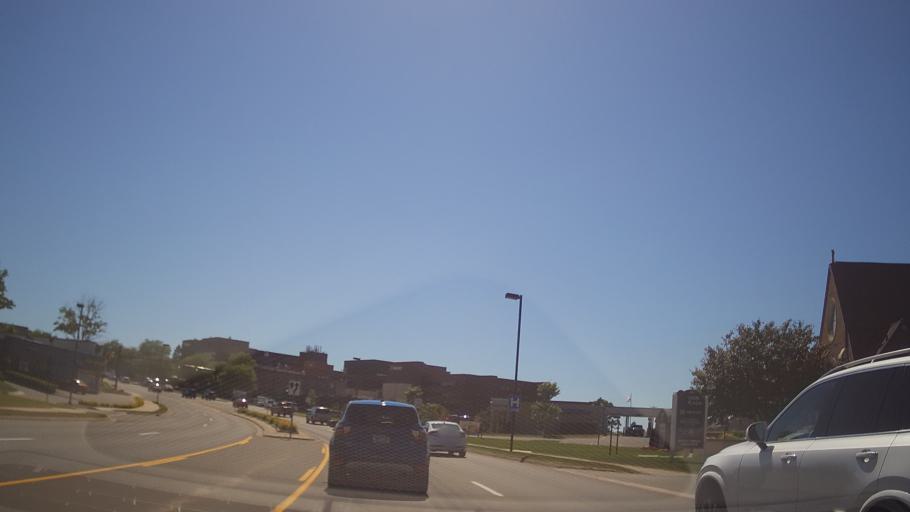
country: US
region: Michigan
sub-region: Emmet County
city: Petoskey
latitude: 45.3740
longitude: -84.9670
